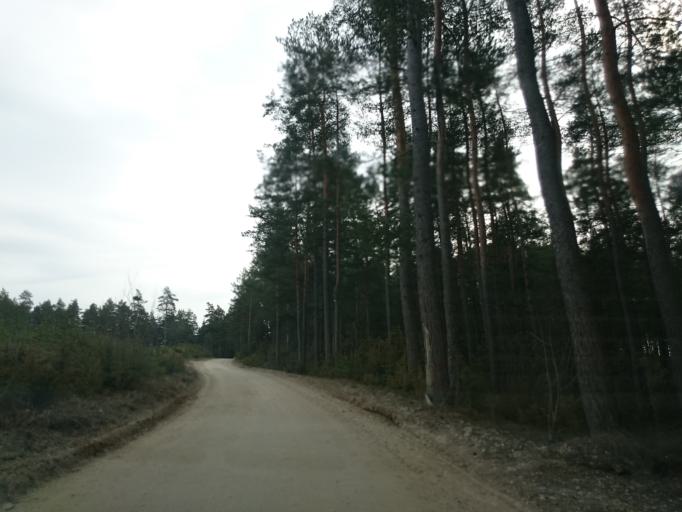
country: LV
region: Garkalne
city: Garkalne
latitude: 57.0327
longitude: 24.3814
